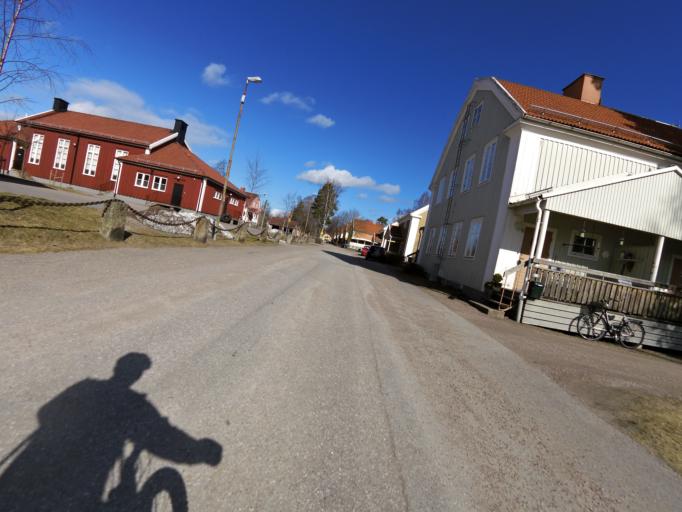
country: SE
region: Gaevleborg
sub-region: Hofors Kommun
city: Hofors
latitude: 60.5451
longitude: 16.2899
